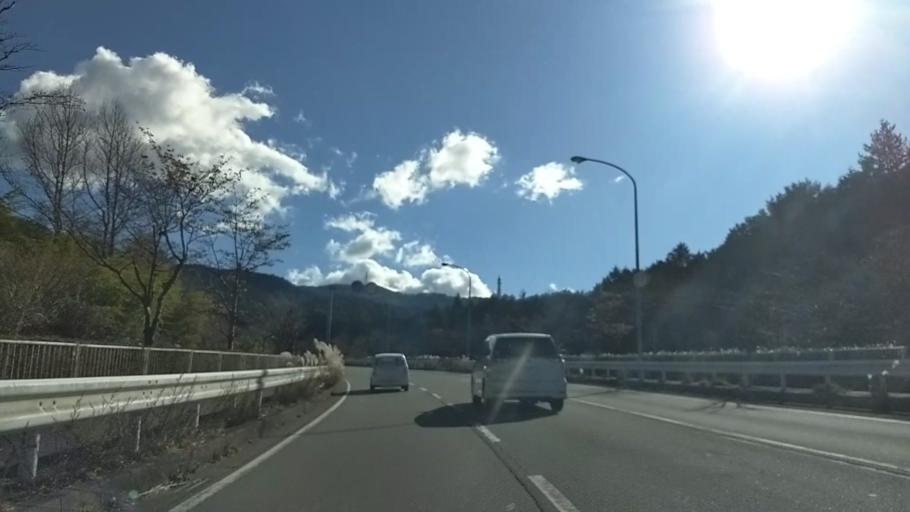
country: JP
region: Shizuoka
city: Gotemba
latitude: 35.2881
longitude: 138.9554
